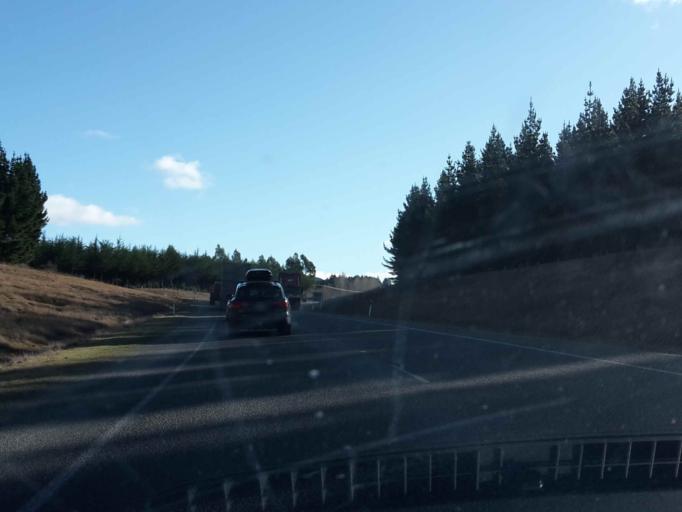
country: NZ
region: Otago
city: Oamaru
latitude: -45.2479
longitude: 170.7917
